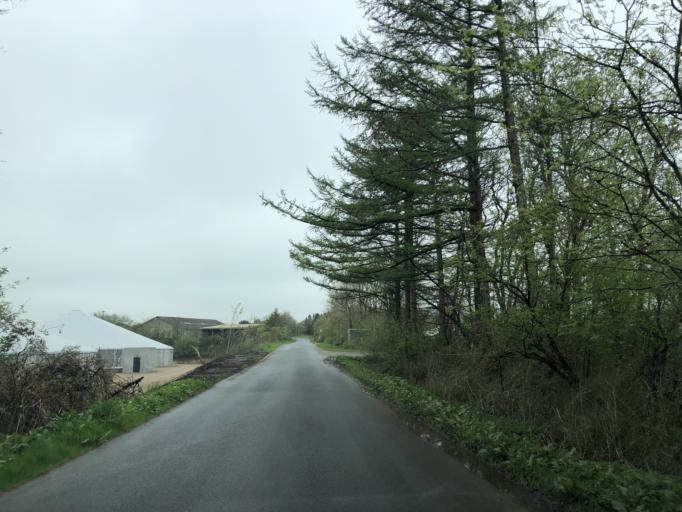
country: DK
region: Central Jutland
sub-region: Lemvig Kommune
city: Lemvig
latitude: 56.5119
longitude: 8.3142
